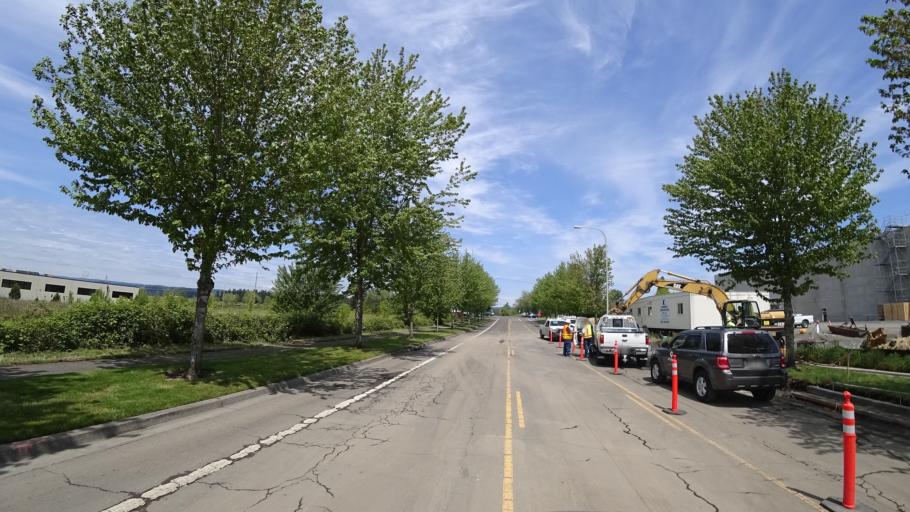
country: US
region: Oregon
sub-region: Washington County
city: Rockcreek
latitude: 45.5723
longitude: -122.9077
